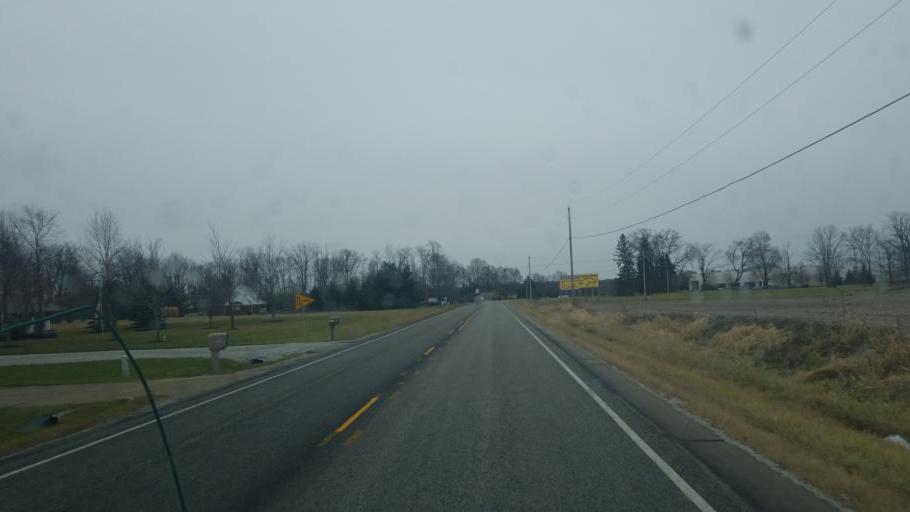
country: US
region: Indiana
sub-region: Henry County
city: Knightstown
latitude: 39.8242
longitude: -85.5363
